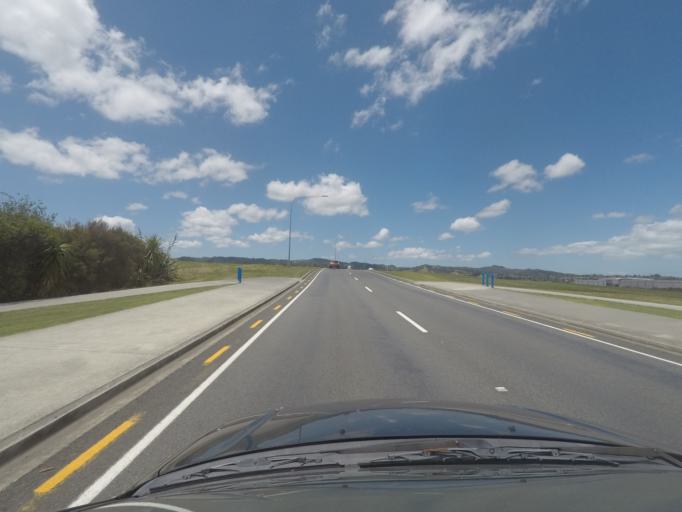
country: NZ
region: Northland
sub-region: Whangarei
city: Whangarei
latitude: -35.7348
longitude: 174.3374
